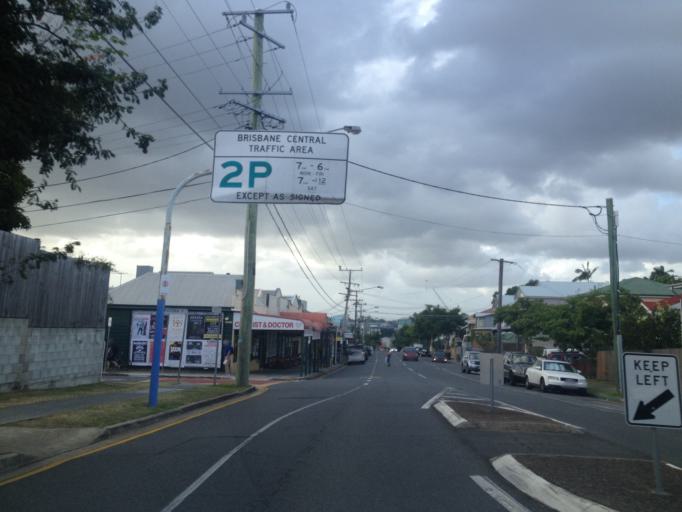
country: AU
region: Queensland
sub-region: Brisbane
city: Milton
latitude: -27.4835
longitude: 153.0068
